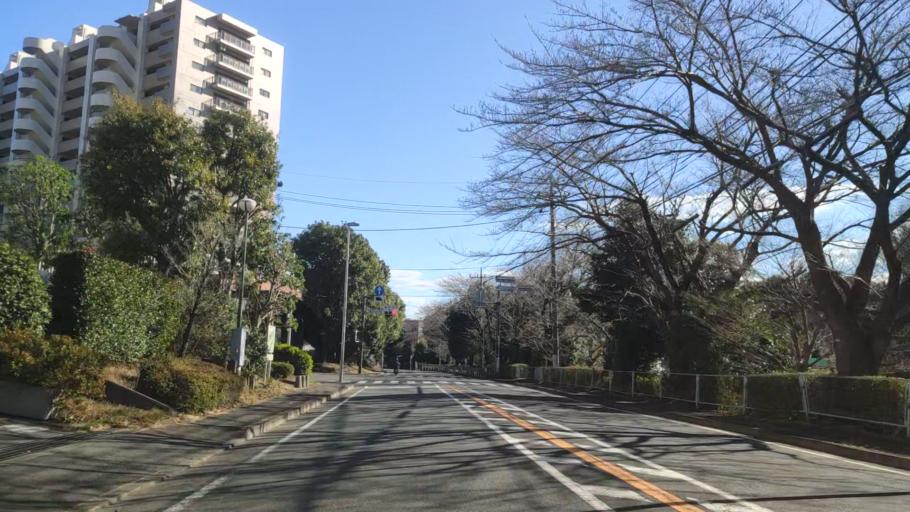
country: JP
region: Kanagawa
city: Minami-rinkan
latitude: 35.5031
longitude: 139.4944
